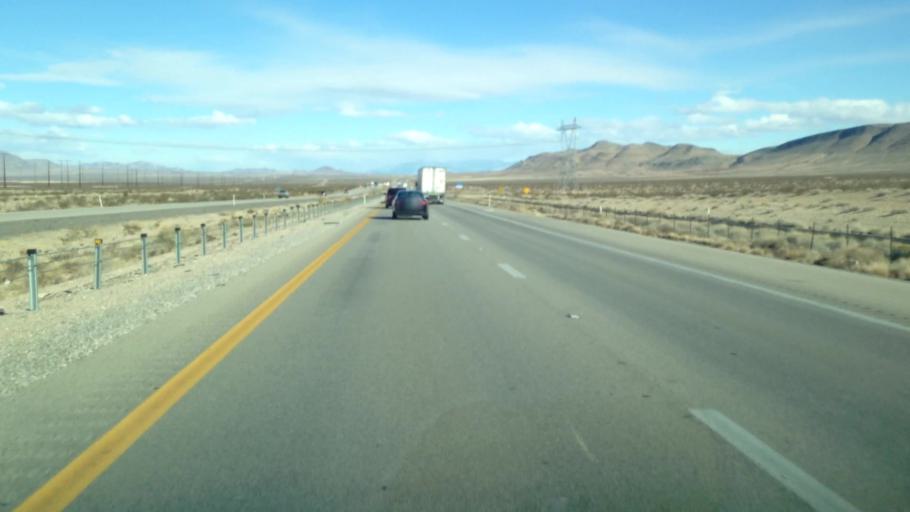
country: US
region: Nevada
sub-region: Clark County
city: Nellis Air Force Base
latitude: 36.4000
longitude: -114.8770
